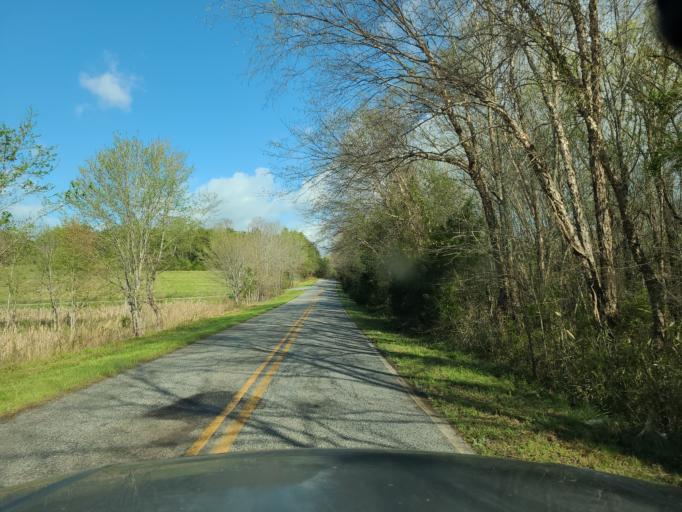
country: US
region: North Carolina
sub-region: Rutherford County
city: Forest City
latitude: 35.4208
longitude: -81.8220
